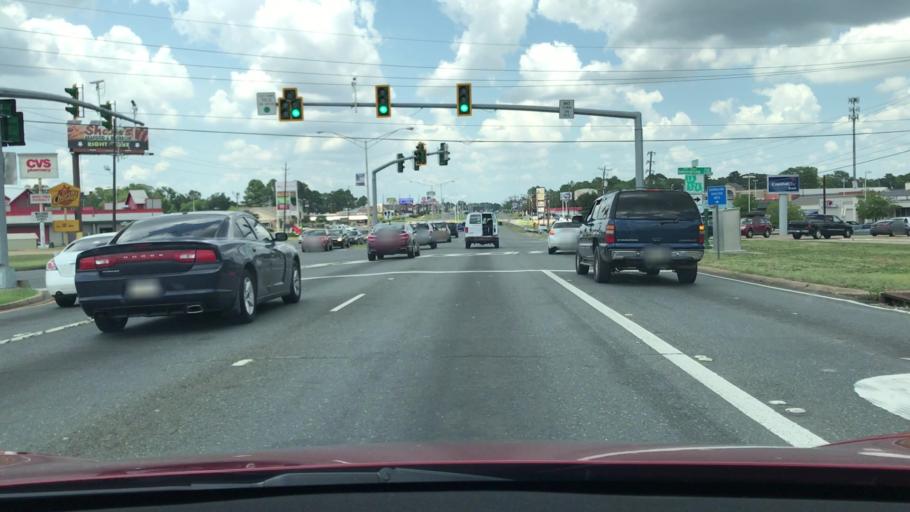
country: US
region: Louisiana
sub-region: De Soto Parish
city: Stonewall
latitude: 32.4017
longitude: -93.8045
